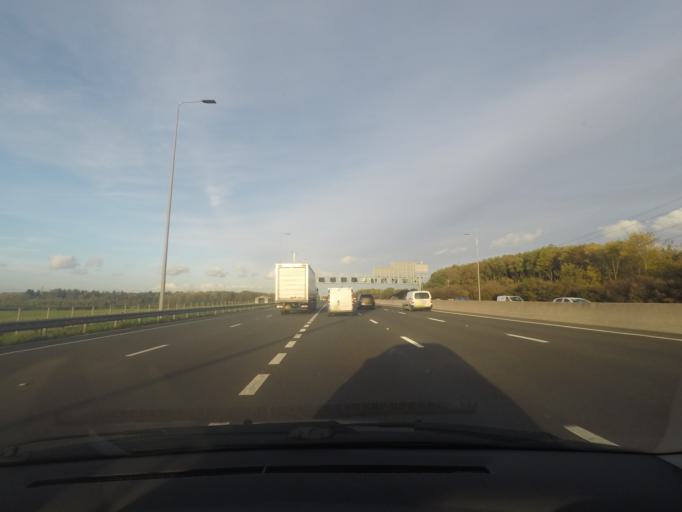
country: GB
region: England
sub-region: City and Borough of Leeds
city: Lofthouse
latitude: 53.7218
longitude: -1.5237
